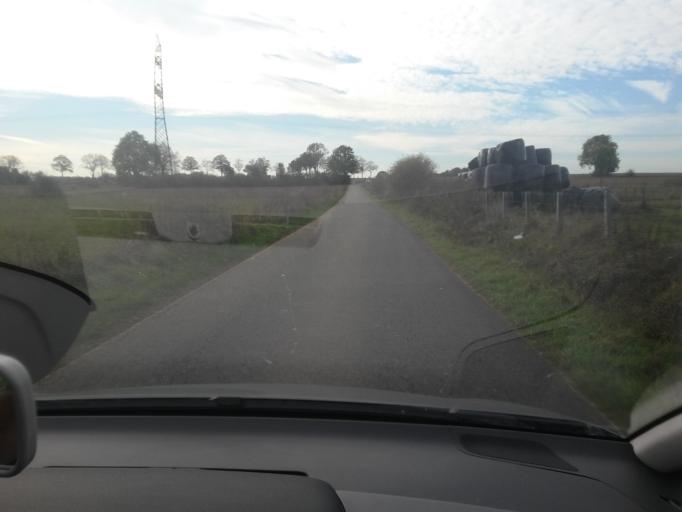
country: BE
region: Wallonia
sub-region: Province du Luxembourg
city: Attert
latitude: 49.7072
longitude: 5.7197
